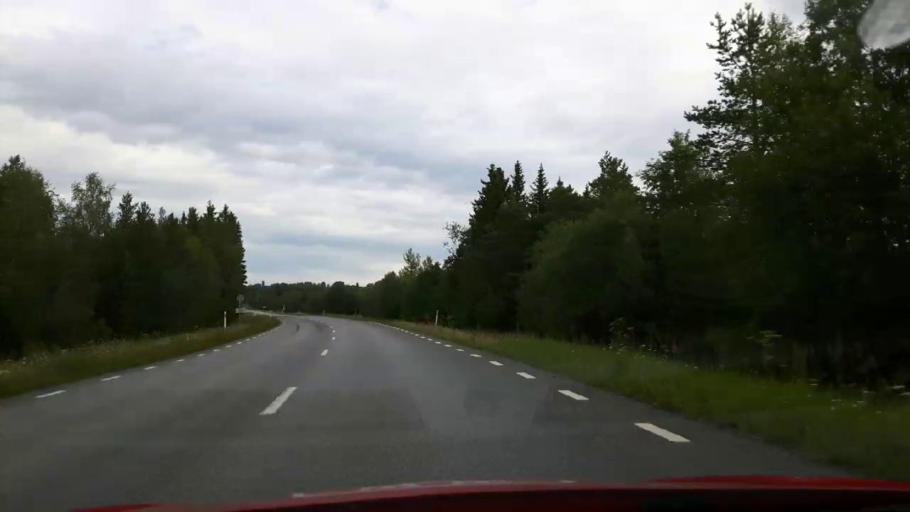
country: SE
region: Jaemtland
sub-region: Stroemsunds Kommun
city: Stroemsund
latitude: 63.5455
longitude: 15.3713
